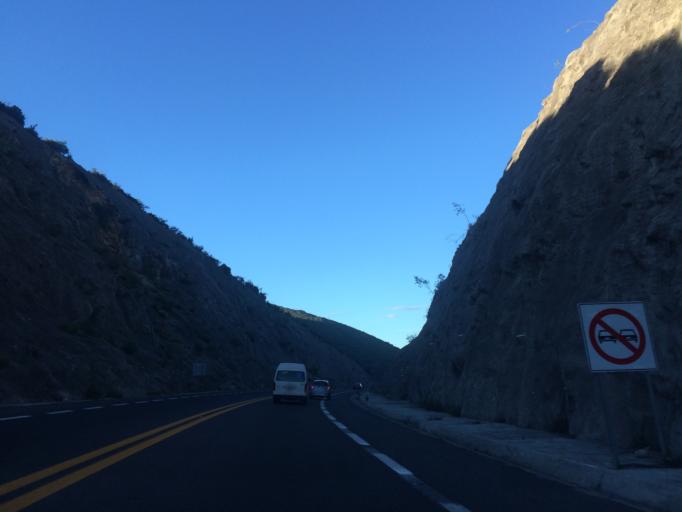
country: MX
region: Puebla
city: Chapuco
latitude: 18.6522
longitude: -97.4525
